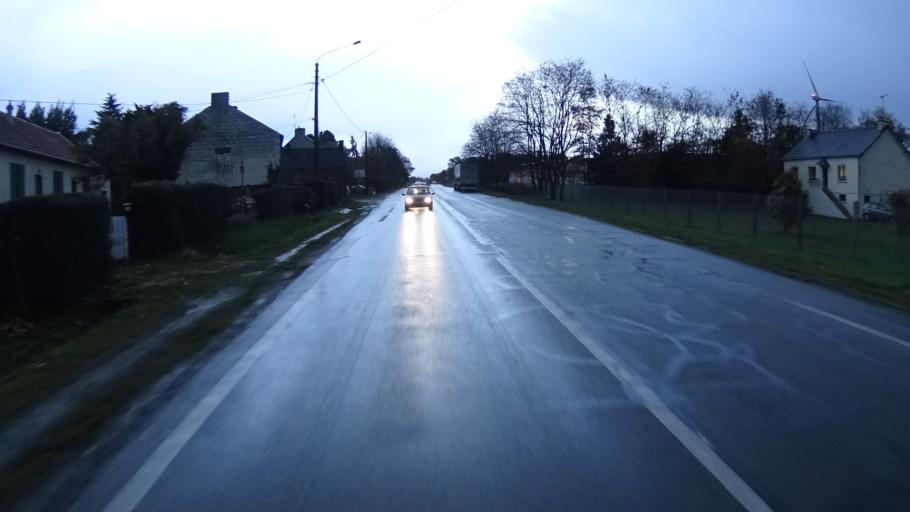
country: FR
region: Brittany
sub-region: Departement d'Ille-et-Vilaine
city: Bains-sur-Oust
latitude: 47.6804
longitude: -2.0599
